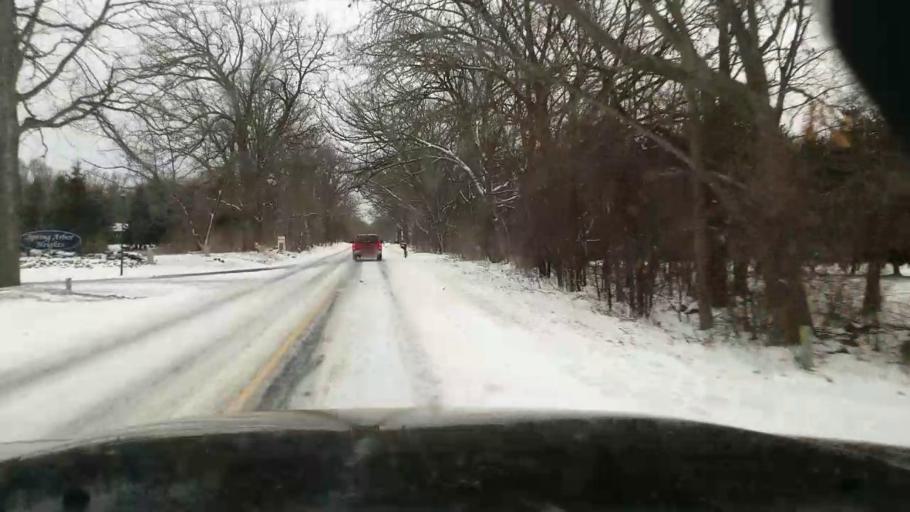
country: US
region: Michigan
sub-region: Jackson County
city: Spring Arbor
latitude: 42.1768
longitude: -84.5007
